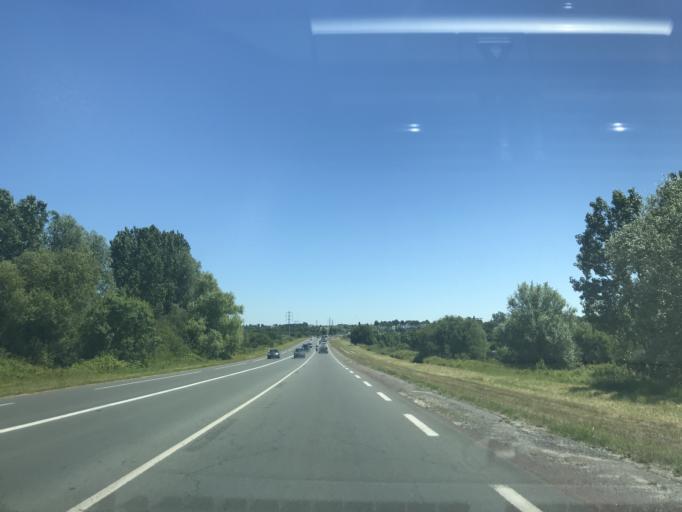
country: FR
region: Poitou-Charentes
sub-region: Departement de la Charente-Maritime
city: Saint-Georges-de-Didonne
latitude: 45.6213
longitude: -0.9951
